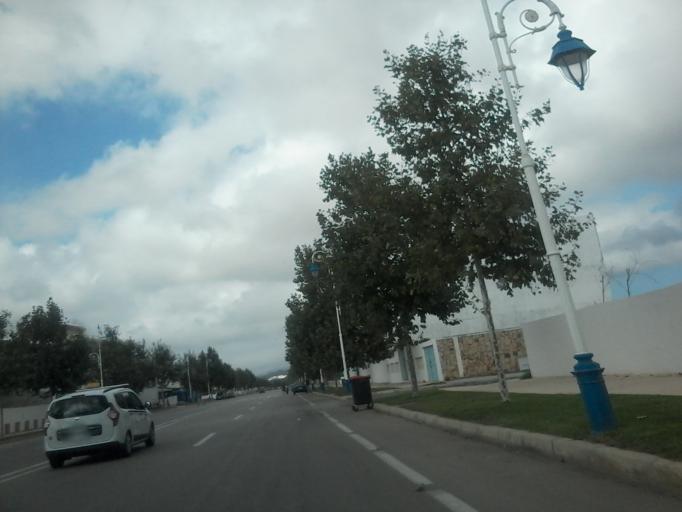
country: MA
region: Tanger-Tetouan
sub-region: Tetouan
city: Martil
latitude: 35.6367
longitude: -5.2890
